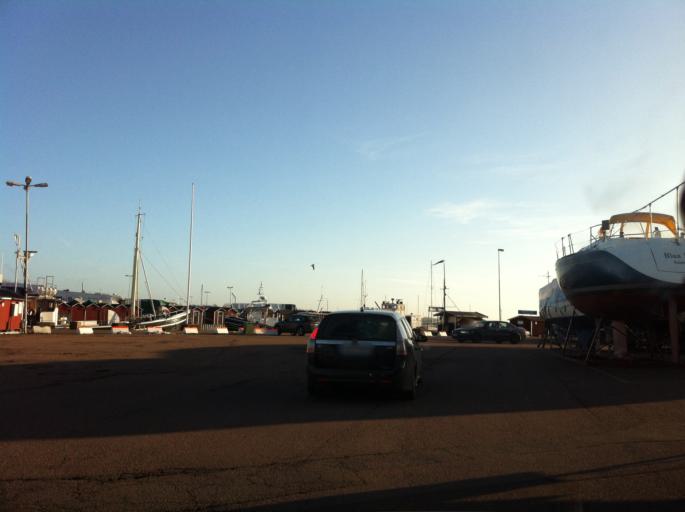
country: SE
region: Skane
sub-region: Helsingborg
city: Rydeback
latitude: 55.9934
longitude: 12.7432
